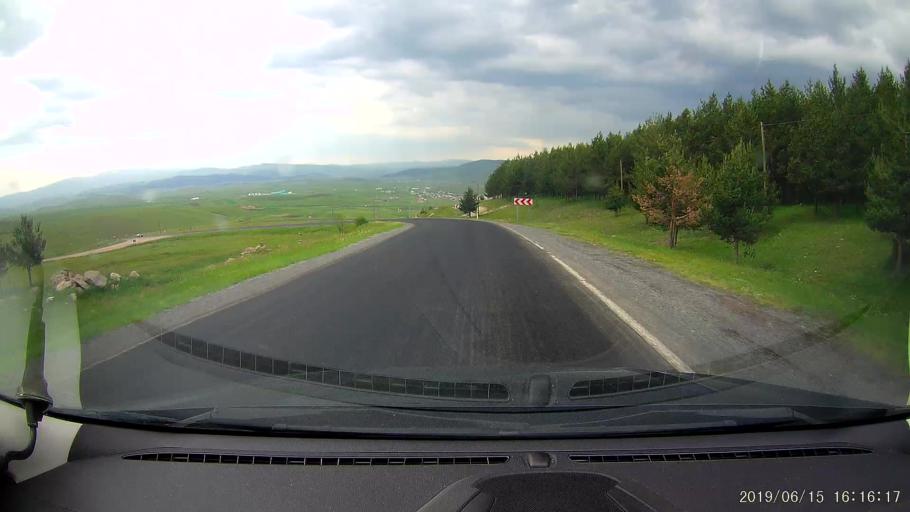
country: TR
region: Ardahan
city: Hanak
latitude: 41.2601
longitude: 42.8525
